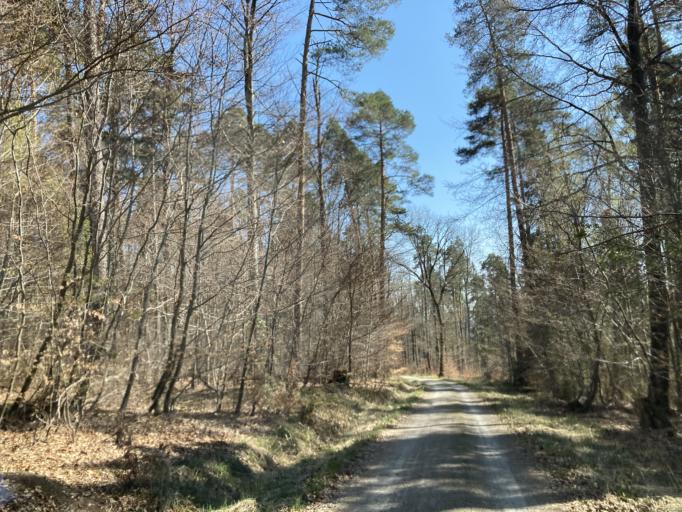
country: DE
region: Baden-Wuerttemberg
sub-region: Tuebingen Region
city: Tuebingen
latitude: 48.5708
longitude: 9.0158
